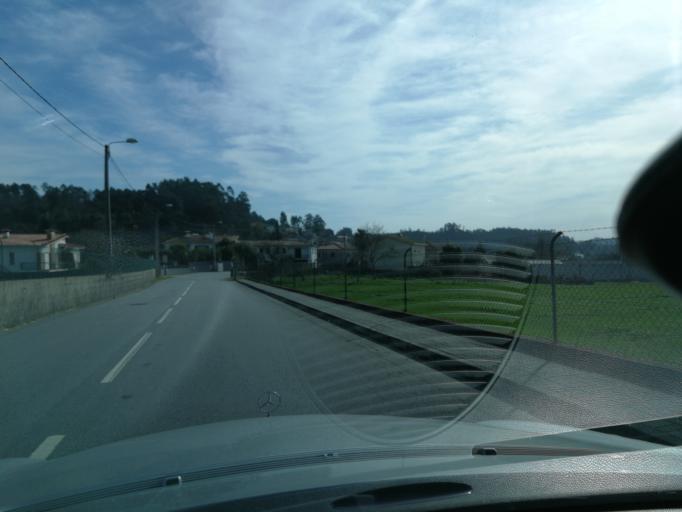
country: PT
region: Braga
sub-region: Vila Nova de Famalicao
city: Vila Nova de Famalicao
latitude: 41.4367
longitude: -8.5219
